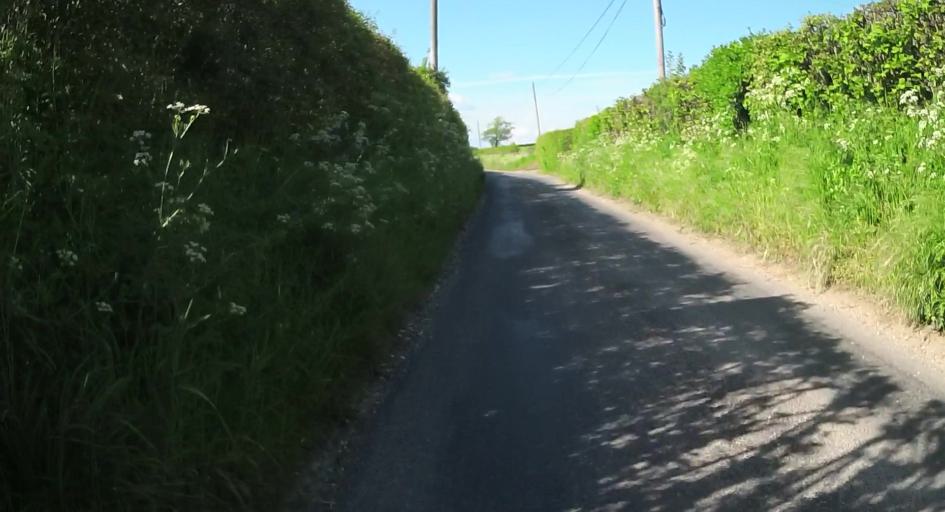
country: GB
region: England
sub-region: Hampshire
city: Kings Worthy
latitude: 51.0966
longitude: -1.2368
